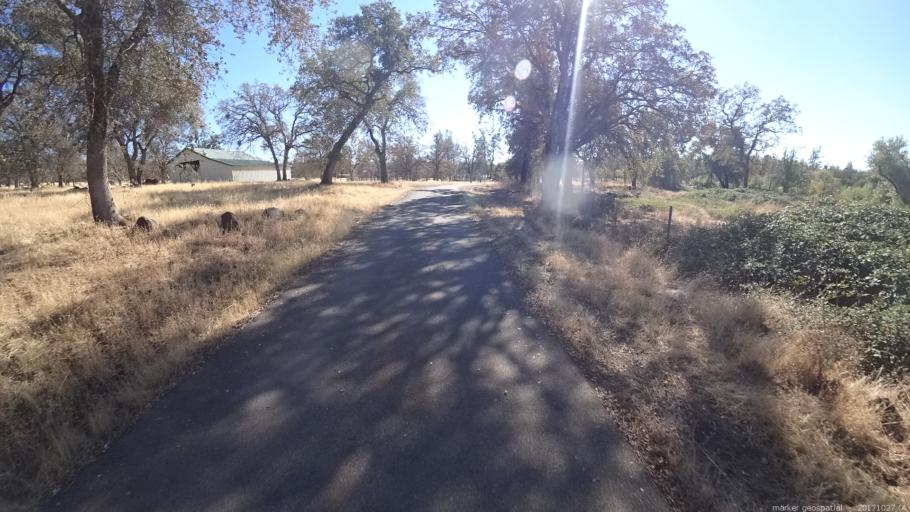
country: US
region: California
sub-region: Shasta County
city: Bella Vista
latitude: 40.6933
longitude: -122.0309
